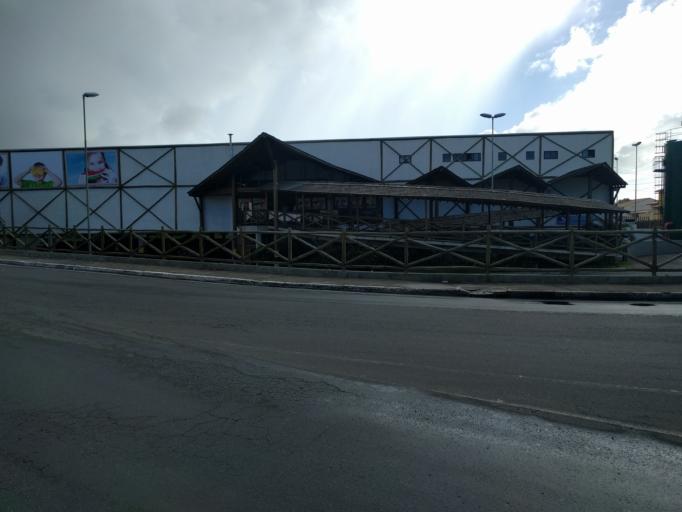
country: BR
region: Bahia
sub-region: Lauro De Freitas
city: Lauro de Freitas
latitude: -12.9428
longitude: -38.3382
